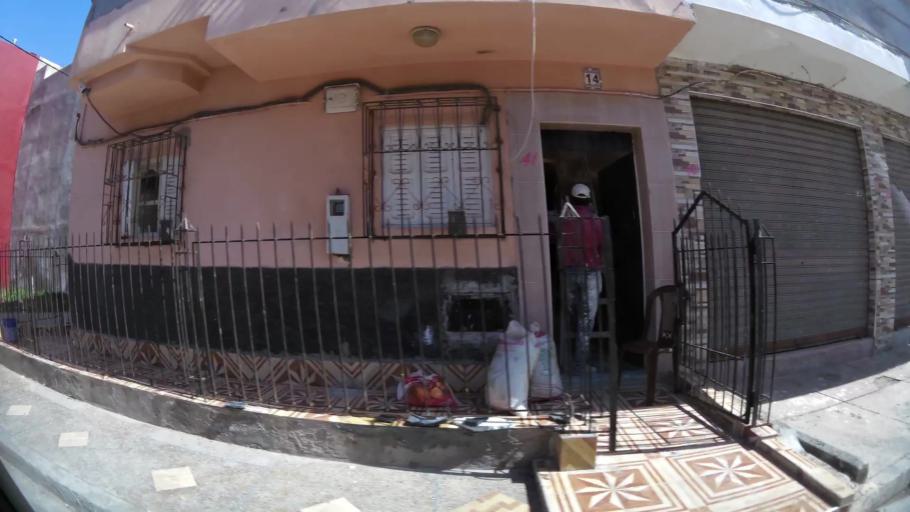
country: MA
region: Souss-Massa-Draa
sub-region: Inezgane-Ait Mellou
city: Inezgane
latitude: 30.3585
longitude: -9.5509
